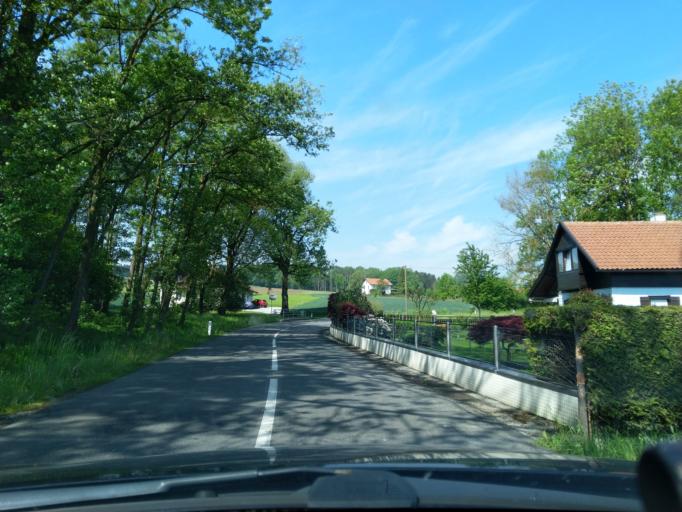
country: AT
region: Upper Austria
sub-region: Politischer Bezirk Scharding
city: Sankt Marienkirchen bei Schaerding
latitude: 48.2963
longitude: 13.4246
